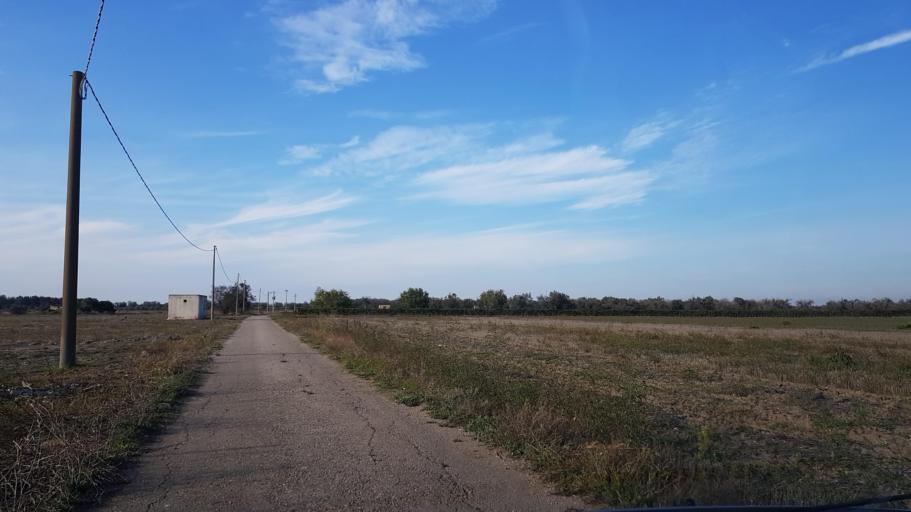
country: IT
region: Apulia
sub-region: Provincia di Brindisi
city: Mesagne
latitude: 40.4995
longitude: 17.8508
